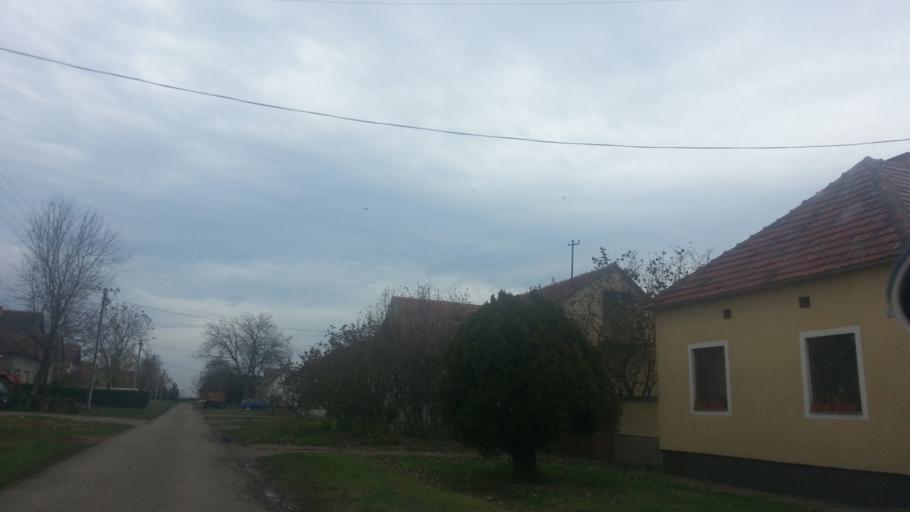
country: RS
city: Golubinci
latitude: 44.9954
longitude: 20.0656
